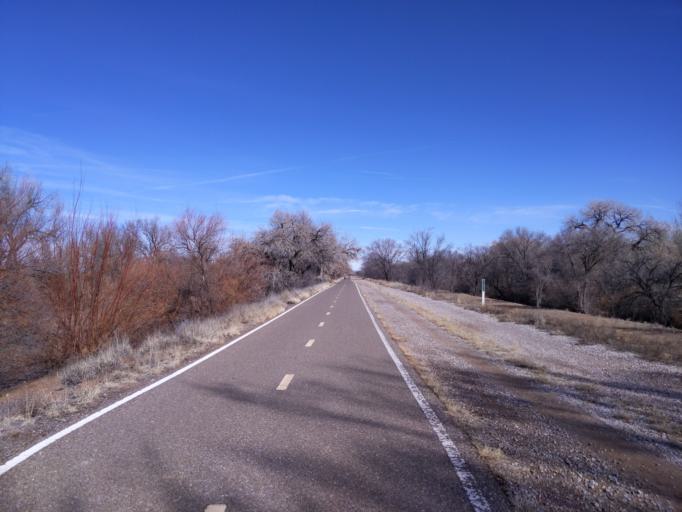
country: US
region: New Mexico
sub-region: Bernalillo County
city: Lee Acres
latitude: 35.1524
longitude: -106.6701
